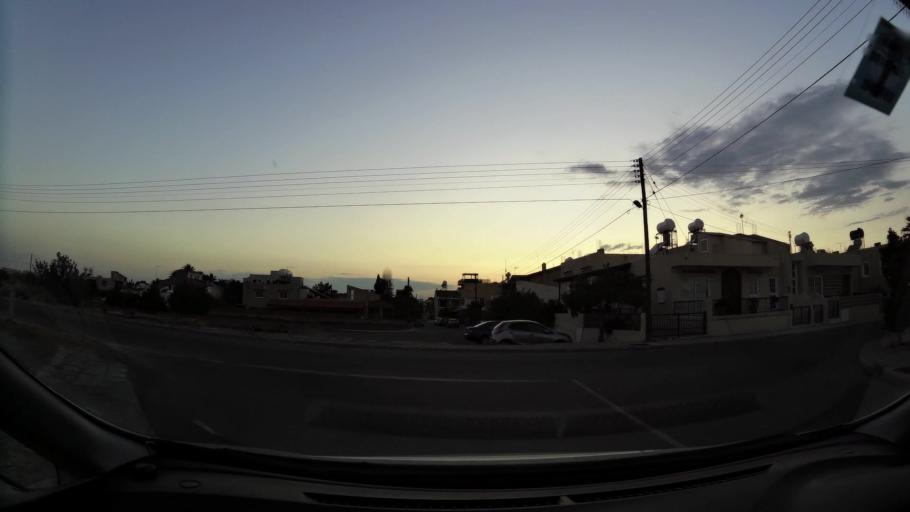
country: CY
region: Larnaka
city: Larnaca
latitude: 34.9153
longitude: 33.5998
